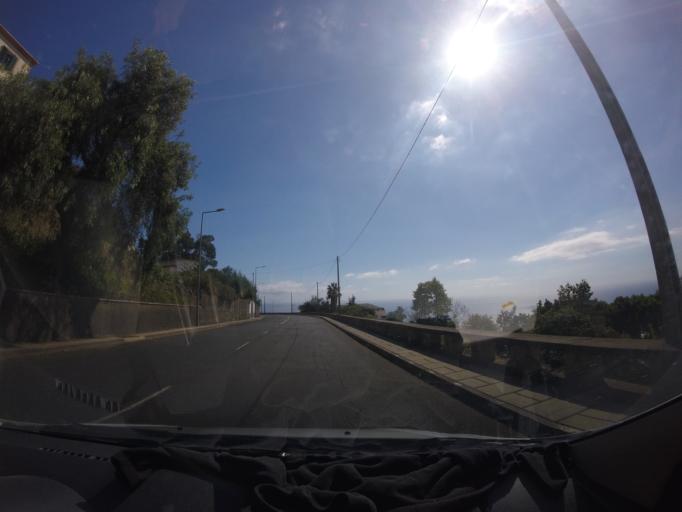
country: PT
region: Madeira
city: Camara de Lobos
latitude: 32.6640
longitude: -16.9488
